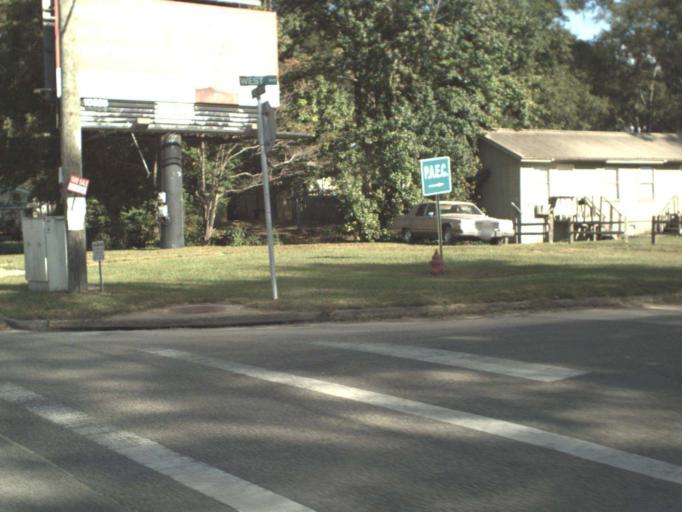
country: US
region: Florida
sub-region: Washington County
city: Chipley
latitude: 30.7773
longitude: -85.5514
